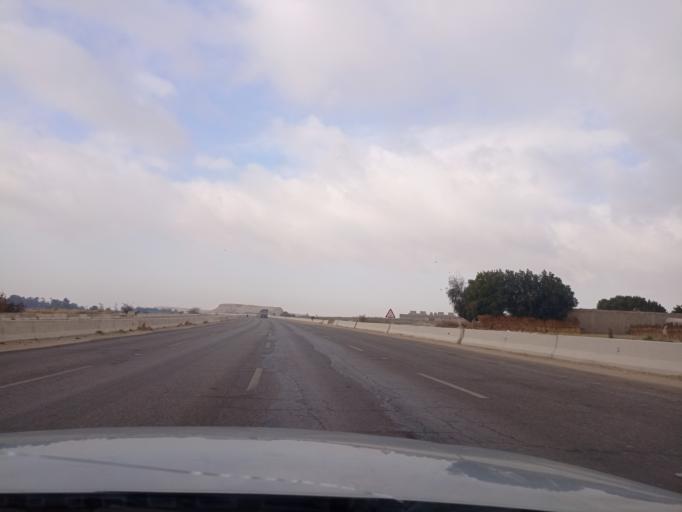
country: EG
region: Al Jizah
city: Al `Ayyat
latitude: 29.6827
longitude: 31.2200
